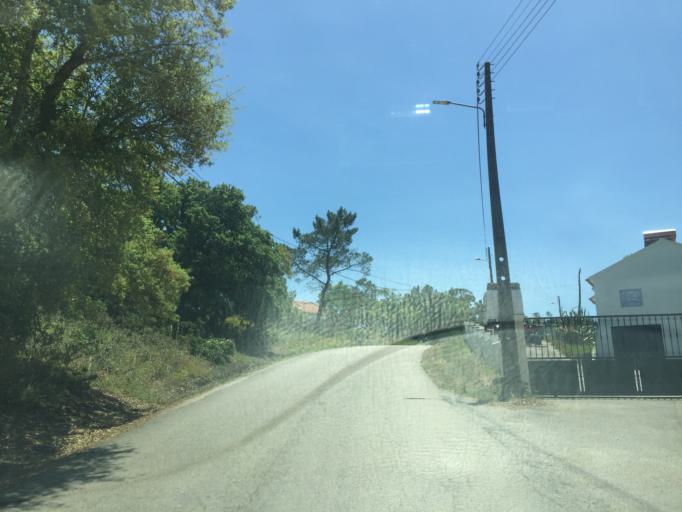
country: PT
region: Lisbon
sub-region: Mafra
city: Venda do Pinheiro
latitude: 38.8955
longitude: -9.2297
